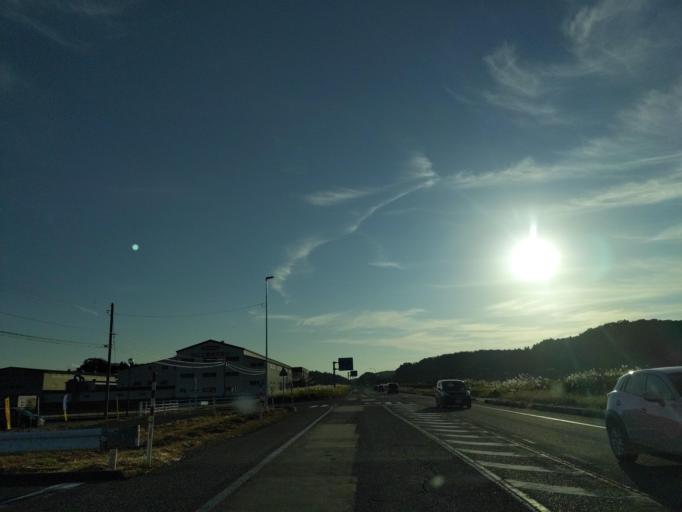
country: JP
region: Niigata
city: Nagaoka
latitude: 37.5733
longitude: 138.7457
